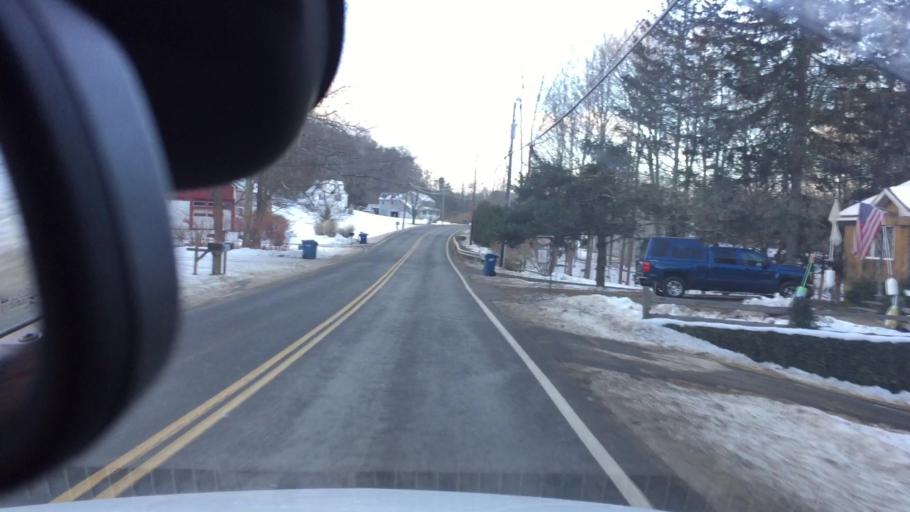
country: US
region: Massachusetts
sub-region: Franklin County
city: Montague
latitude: 42.5007
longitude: -72.5425
